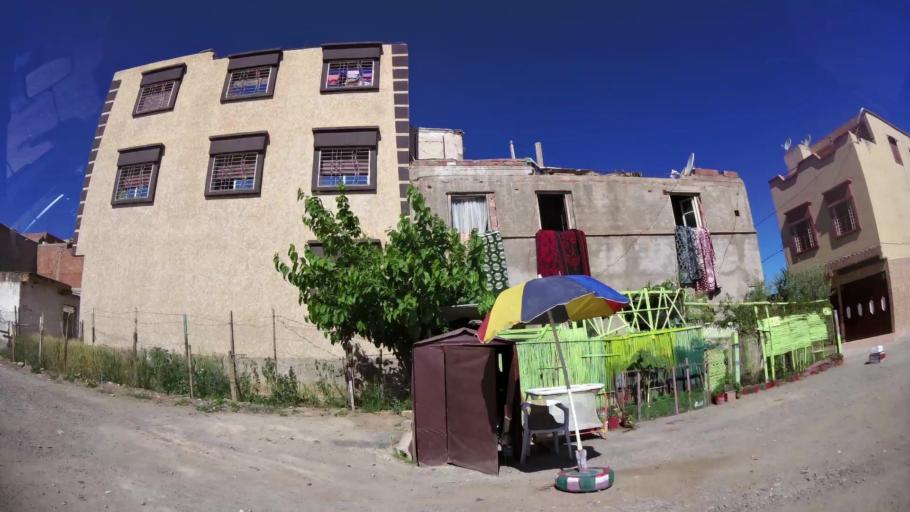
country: MA
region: Oriental
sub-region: Oujda-Angad
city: Oujda
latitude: 34.6494
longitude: -1.8807
